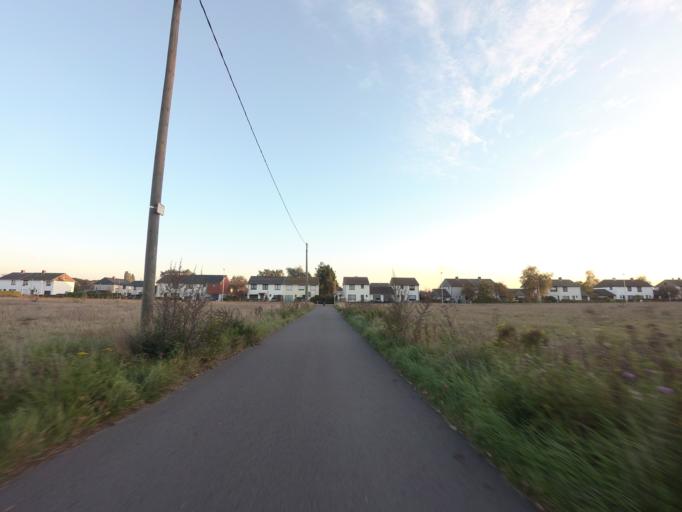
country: BE
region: Flanders
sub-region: Provincie Antwerpen
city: Stabroek
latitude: 51.3493
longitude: 4.3336
